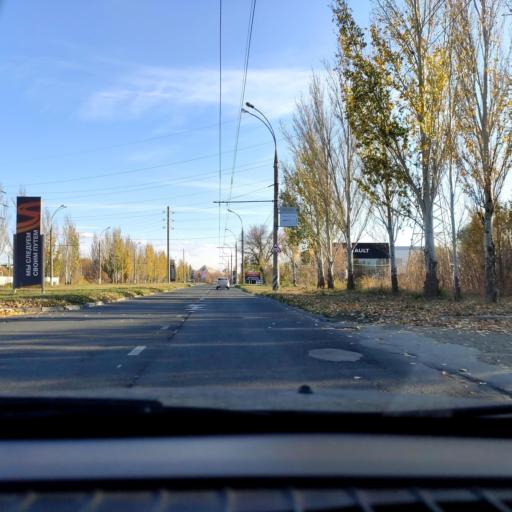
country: RU
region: Samara
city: Tol'yatti
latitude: 53.5469
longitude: 49.2746
